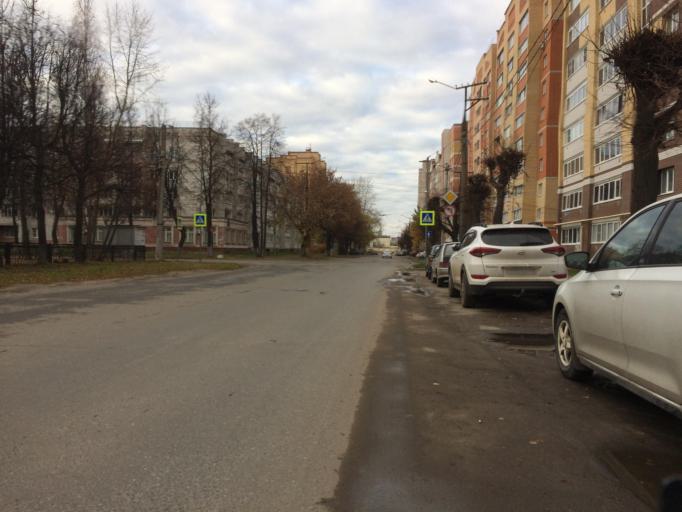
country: RU
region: Mariy-El
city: Yoshkar-Ola
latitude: 56.6406
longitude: 47.8649
